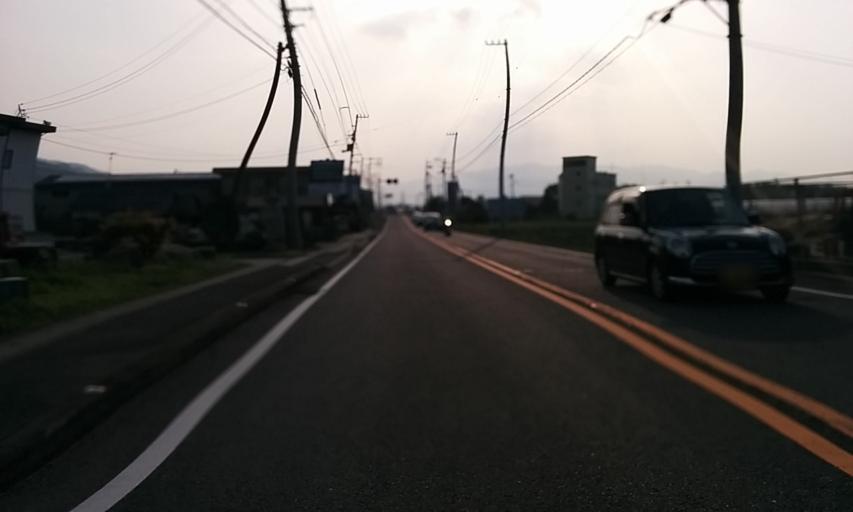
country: JP
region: Ehime
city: Saijo
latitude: 33.8949
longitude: 133.1609
